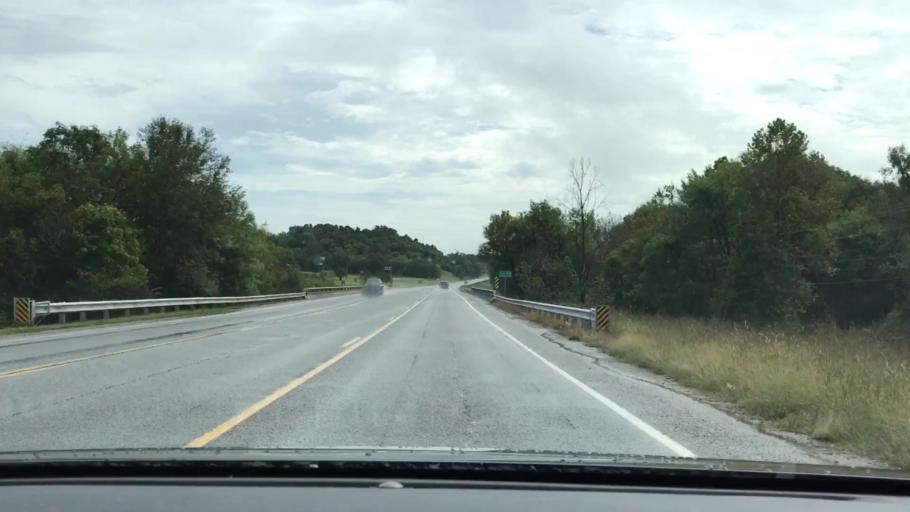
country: US
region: Tennessee
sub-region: Smith County
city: Gordonsville
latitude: 36.1916
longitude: -85.9538
